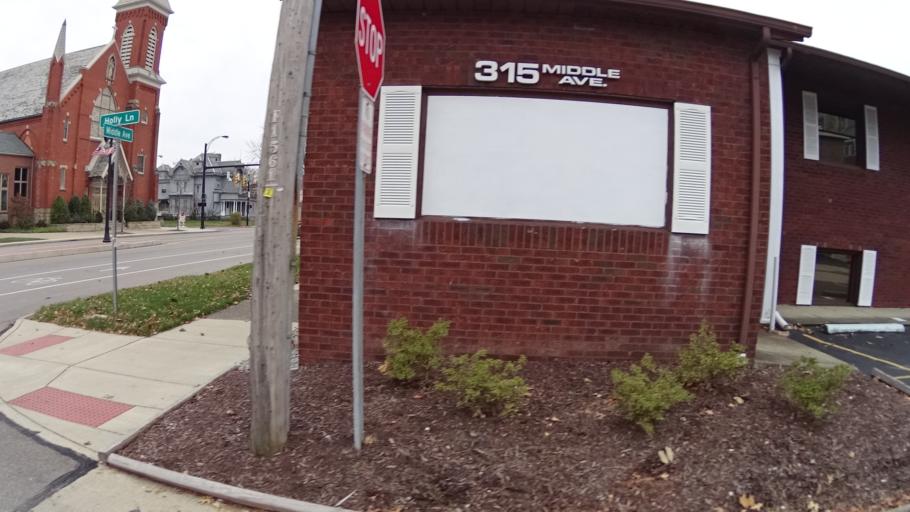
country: US
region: Ohio
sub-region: Lorain County
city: Elyria
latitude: 41.3648
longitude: -82.1073
